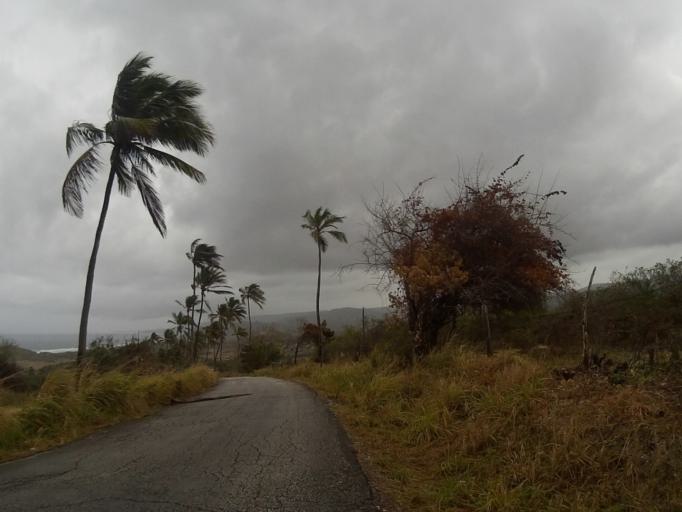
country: BB
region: Saint Andrew
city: Greenland
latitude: 13.2706
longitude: -59.5768
